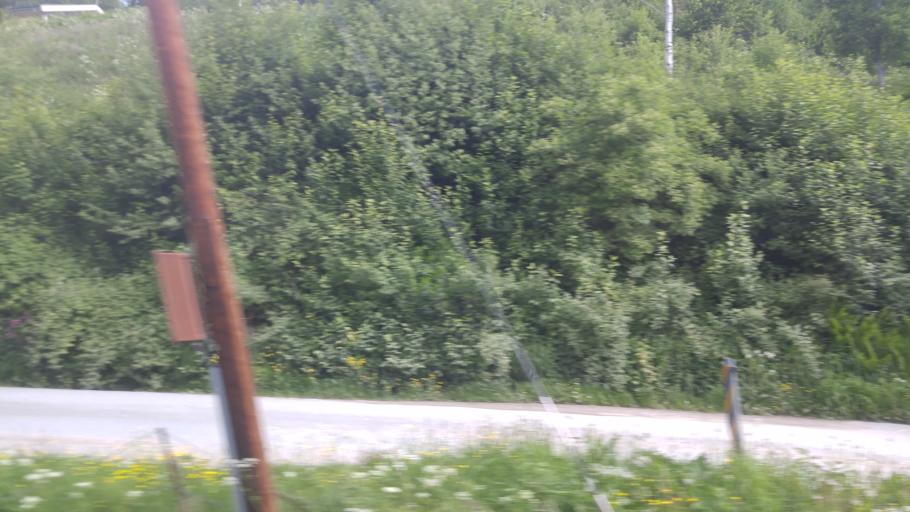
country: NO
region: Sor-Trondelag
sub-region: Midtre Gauldal
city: Storen
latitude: 63.0176
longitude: 10.4445
